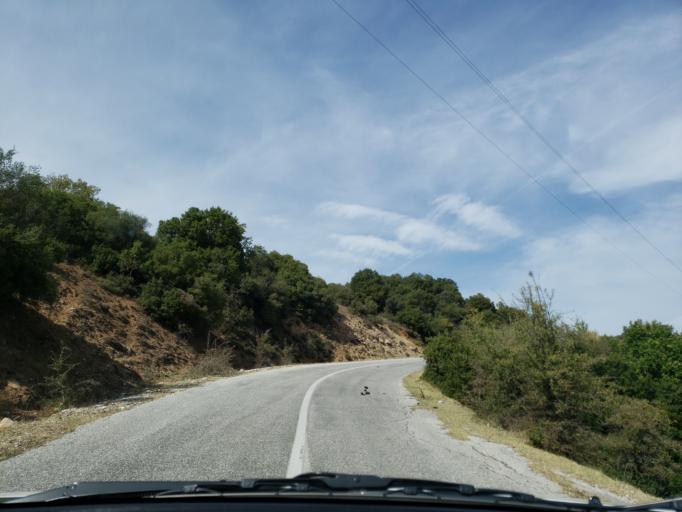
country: GR
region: Thessaly
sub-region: Trikala
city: Kalampaka
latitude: 39.7272
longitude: 21.6484
